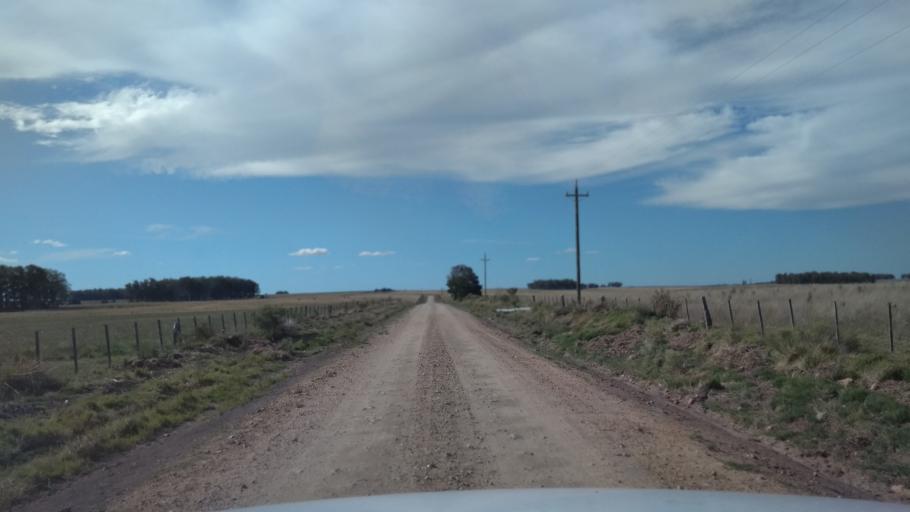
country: UY
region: Florida
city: Casupa
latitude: -34.0309
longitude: -55.7809
